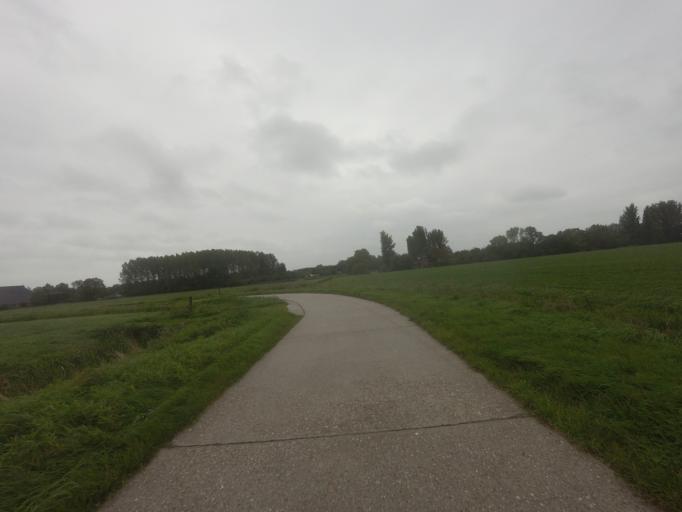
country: NL
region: Friesland
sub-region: Gemeente Leeuwarden
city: Bilgaard
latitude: 53.2272
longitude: 5.7885
